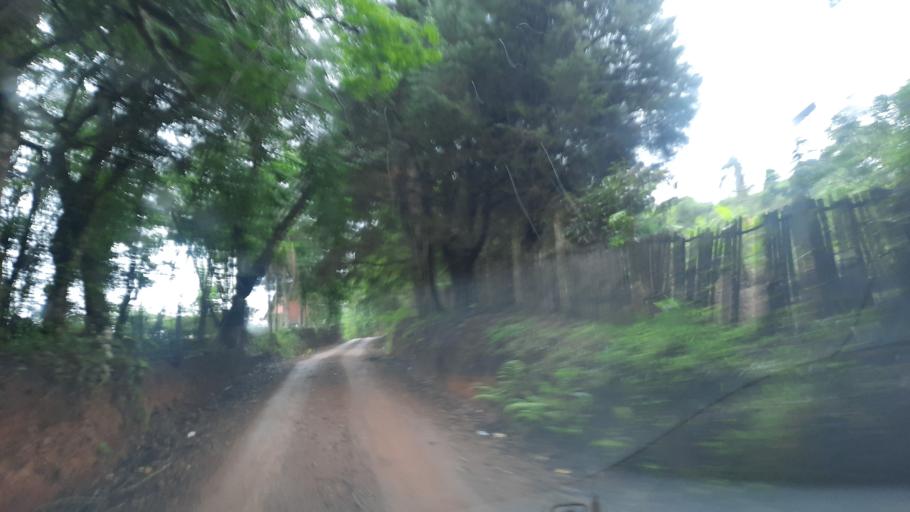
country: BR
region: Sao Paulo
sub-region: Atibaia
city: Atibaia
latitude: -23.0739
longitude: -46.5076
